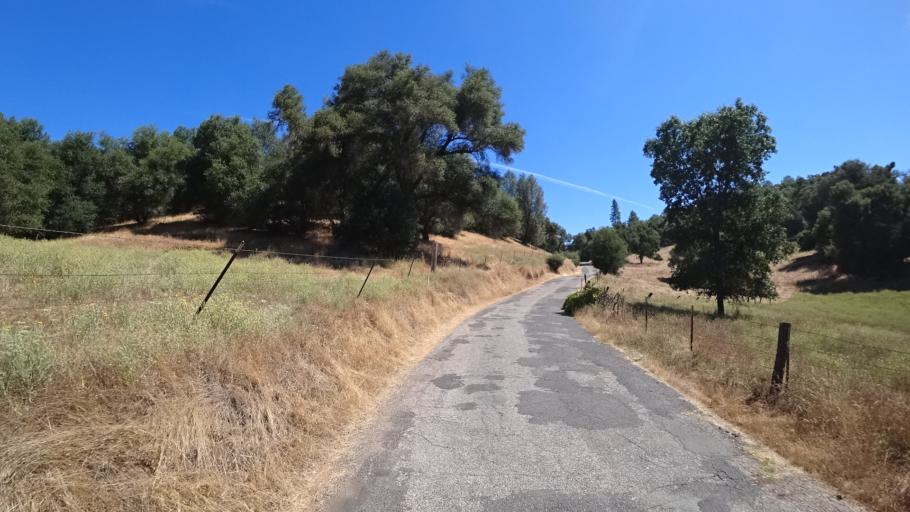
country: US
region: California
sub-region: Calaveras County
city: Angels Camp
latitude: 38.1268
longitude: -120.5716
